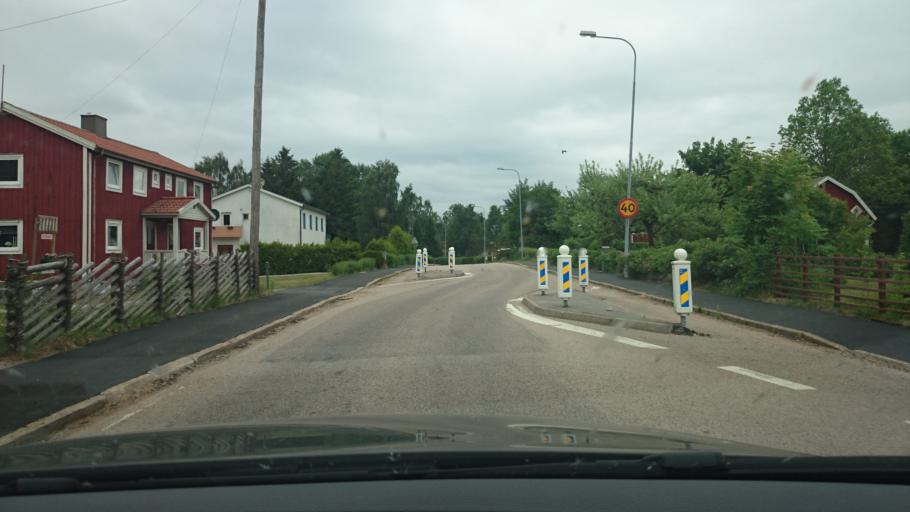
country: SE
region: Halland
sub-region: Hylte Kommun
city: Hyltebruk
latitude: 56.9943
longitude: 13.2332
